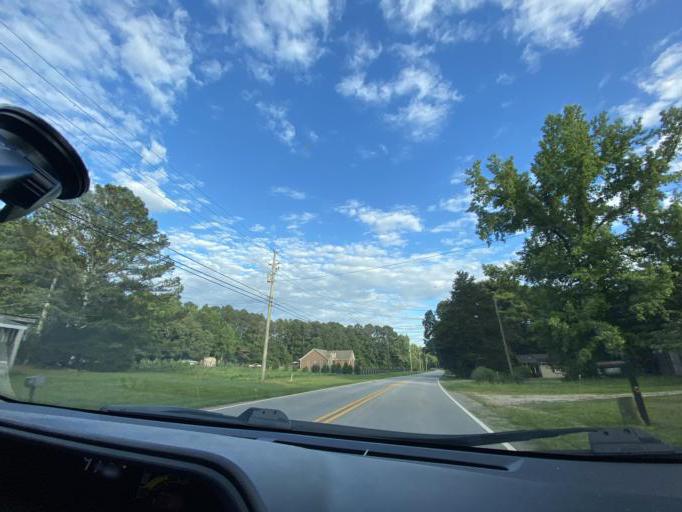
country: US
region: Georgia
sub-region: Fayette County
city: Tyrone
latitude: 33.4410
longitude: -84.6544
